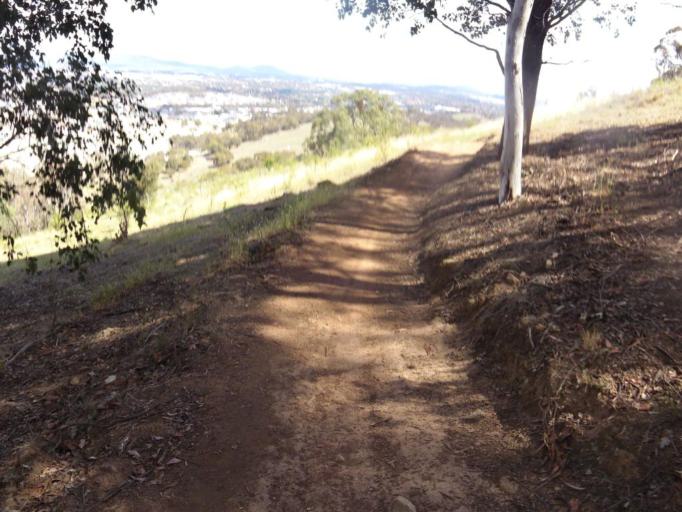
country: AU
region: Australian Capital Territory
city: Belconnen
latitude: -35.1457
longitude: 149.0922
